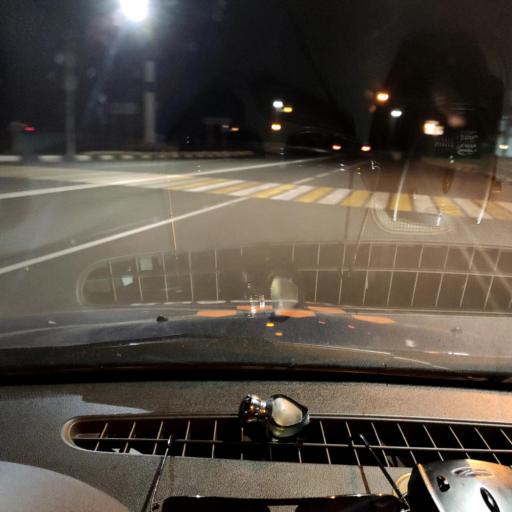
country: RU
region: Belgorod
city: Stroitel'
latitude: 50.7831
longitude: 36.5014
